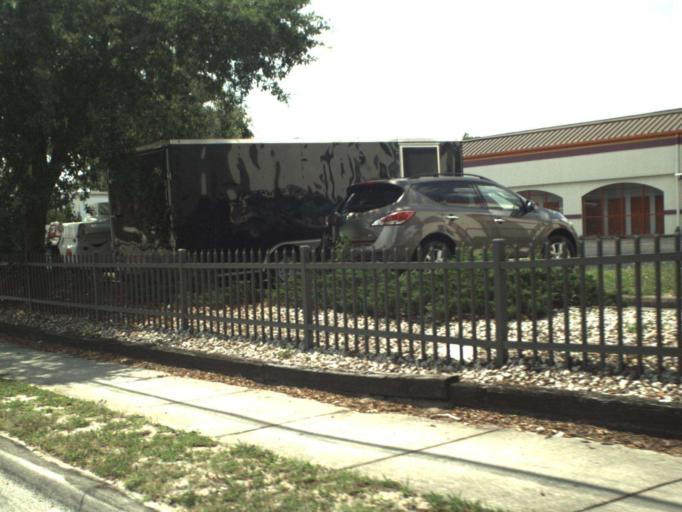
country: US
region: Florida
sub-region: Seminole County
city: Longwood
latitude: 28.6978
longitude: -81.3412
